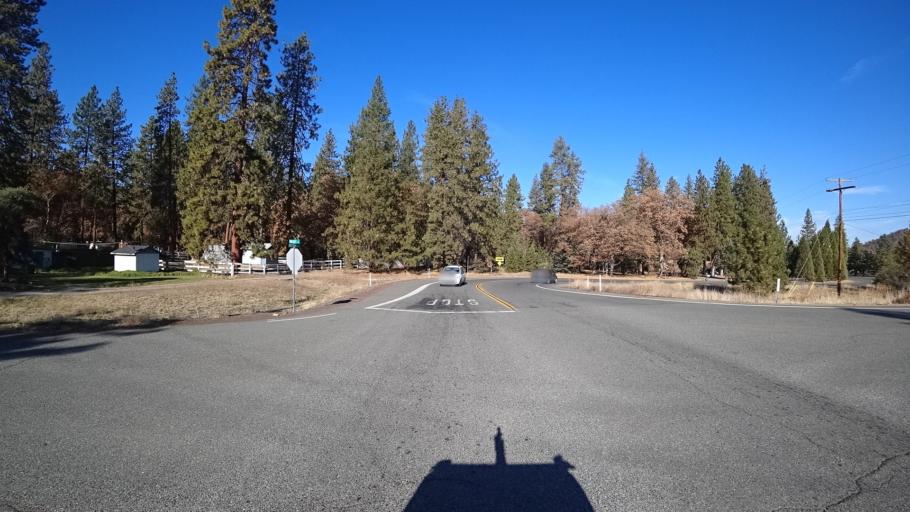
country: US
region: California
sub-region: Siskiyou County
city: Yreka
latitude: 41.6845
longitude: -122.6371
